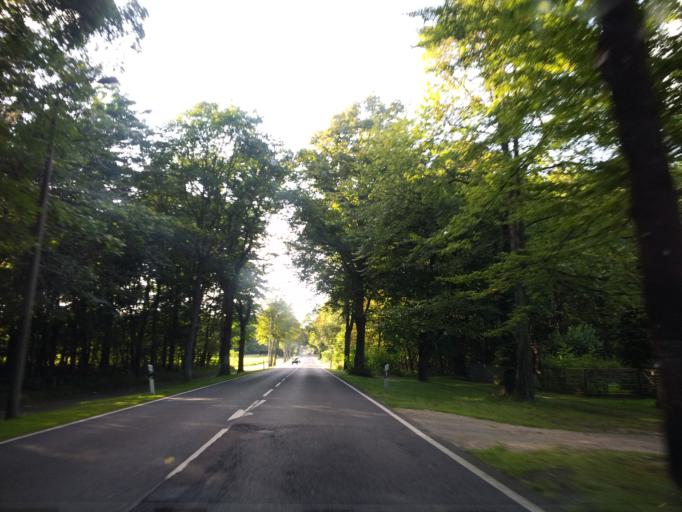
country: DE
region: Brandenburg
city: Niedergorsdorf
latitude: 52.0058
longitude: 13.0177
